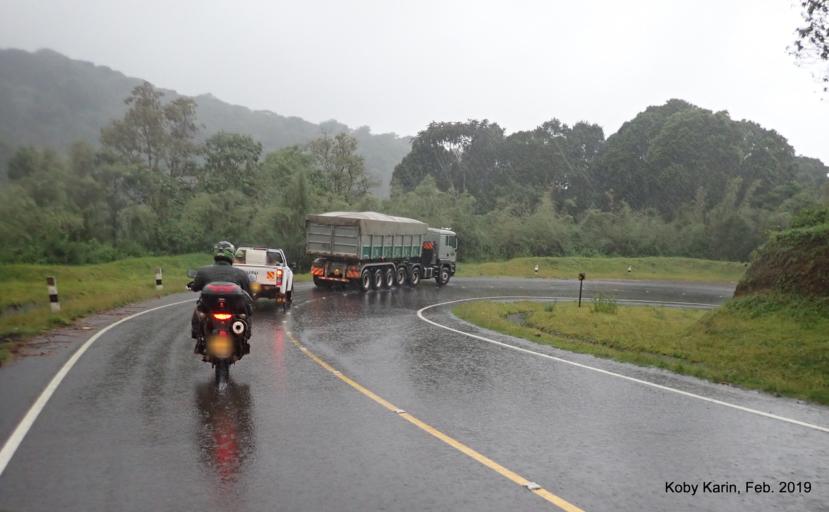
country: UG
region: Western Region
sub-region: Kisoro District
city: Kisoro
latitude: -1.2563
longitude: 29.8063
